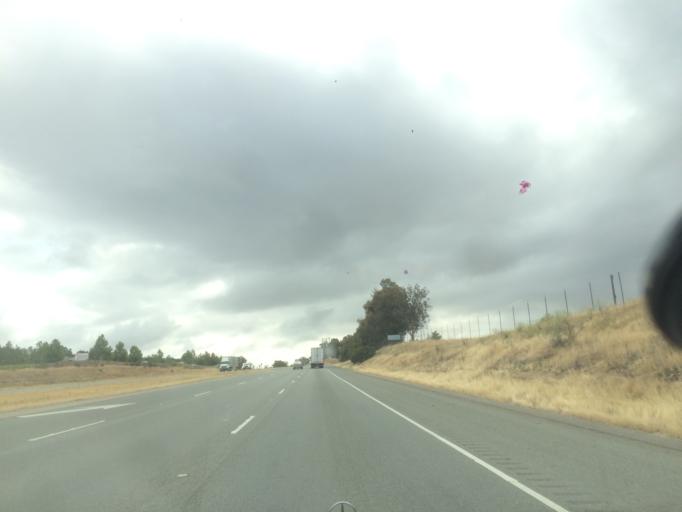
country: US
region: California
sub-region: San Luis Obispo County
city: Paso Robles
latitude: 35.6445
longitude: -120.6420
